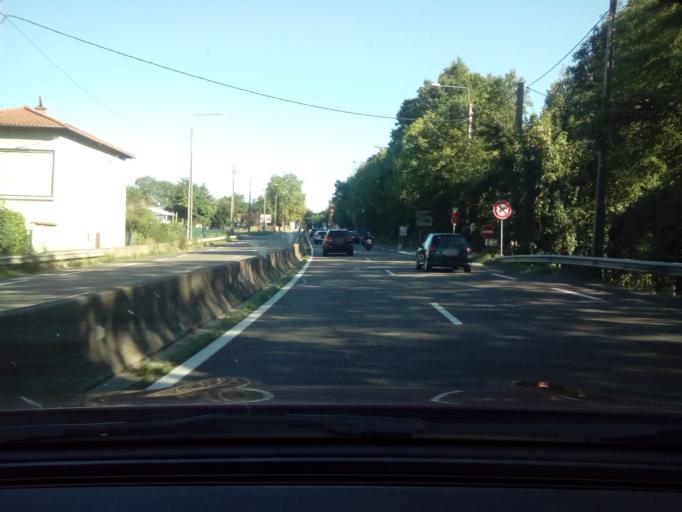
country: FR
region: Rhone-Alpes
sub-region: Departement du Rhone
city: Limonest
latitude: 45.8291
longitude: 4.7534
